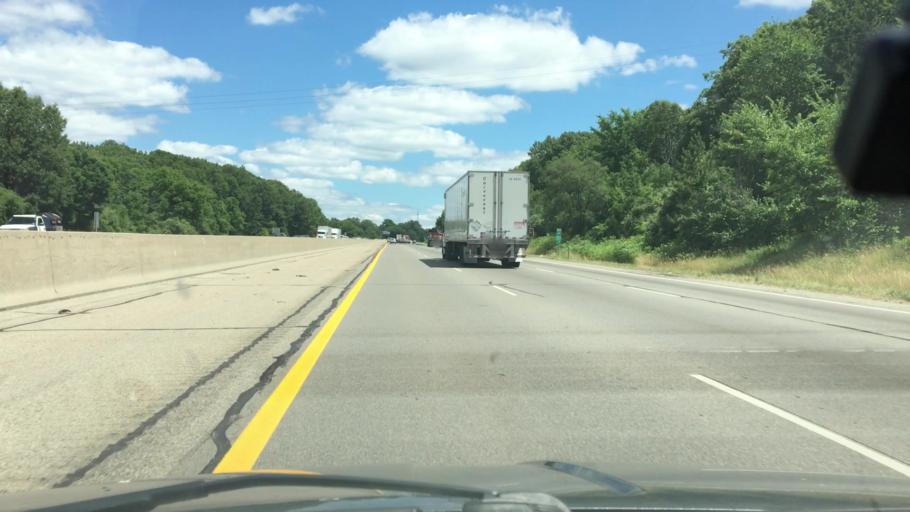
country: US
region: Michigan
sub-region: Oakland County
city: South Lyon
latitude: 42.5196
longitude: -83.6398
